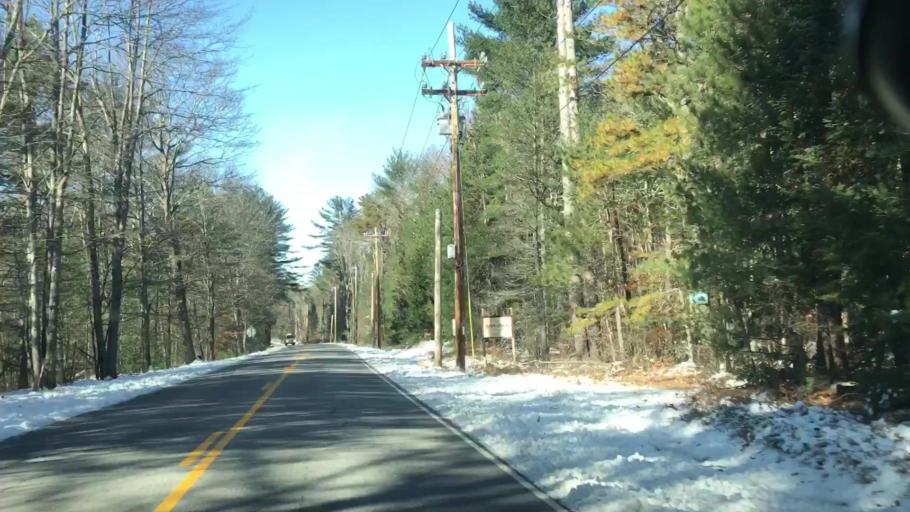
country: US
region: Maine
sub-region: Oxford County
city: Brownfield
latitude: 43.9637
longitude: -70.8637
